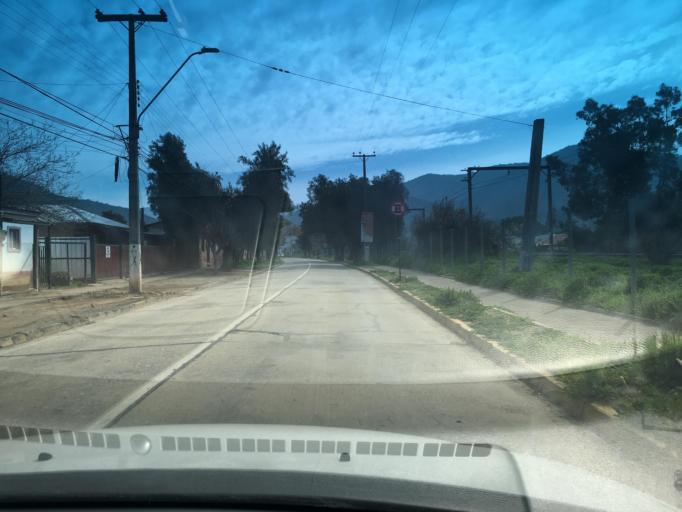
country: CL
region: Santiago Metropolitan
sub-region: Provincia de Chacabuco
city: Lampa
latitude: -33.0779
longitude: -70.9276
